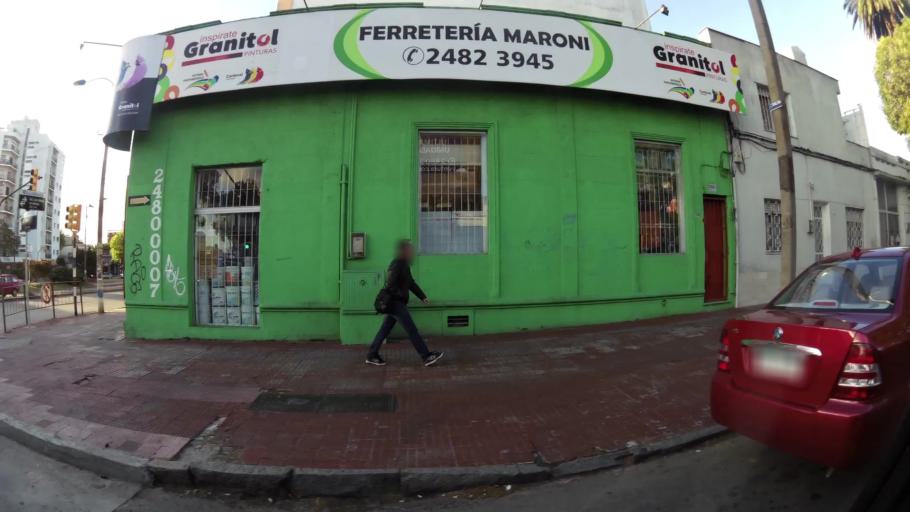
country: UY
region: Montevideo
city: Montevideo
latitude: -34.8827
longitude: -56.1515
